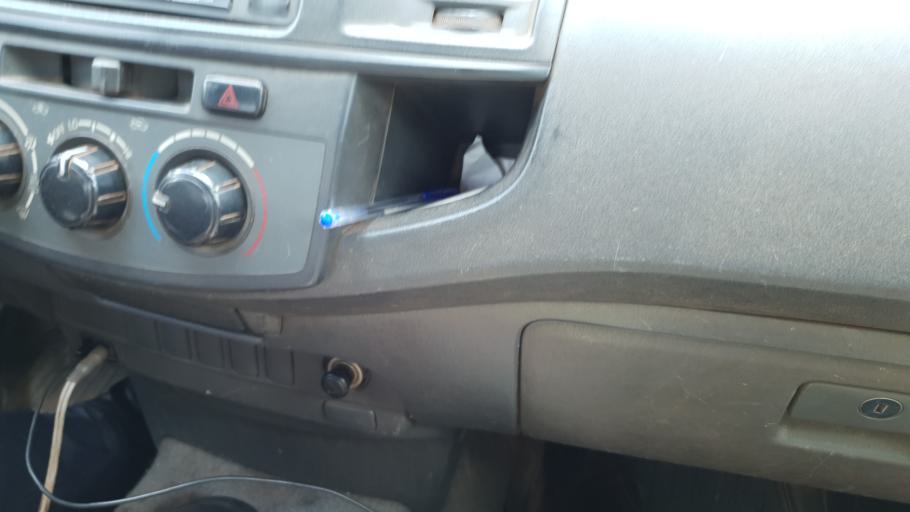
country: ML
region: Segou
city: Baroueli
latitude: 13.3525
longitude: -7.0962
